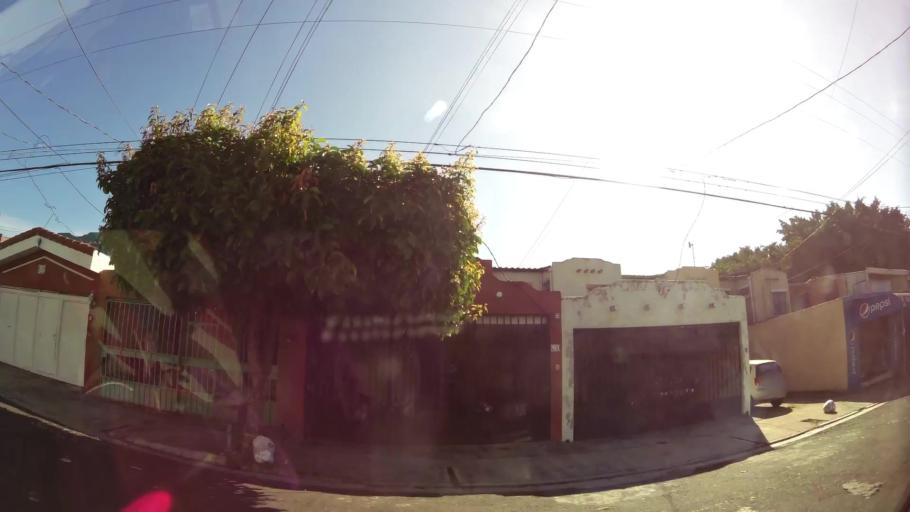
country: SV
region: La Libertad
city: Santa Tecla
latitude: 13.6804
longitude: -89.2984
